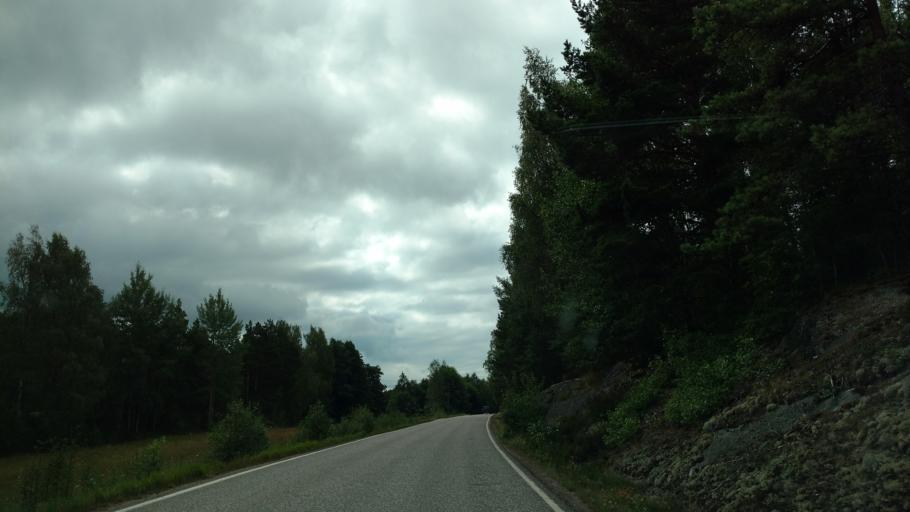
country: FI
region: Varsinais-Suomi
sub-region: Aboland-Turunmaa
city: Dragsfjaerd
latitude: 60.0200
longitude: 22.4593
